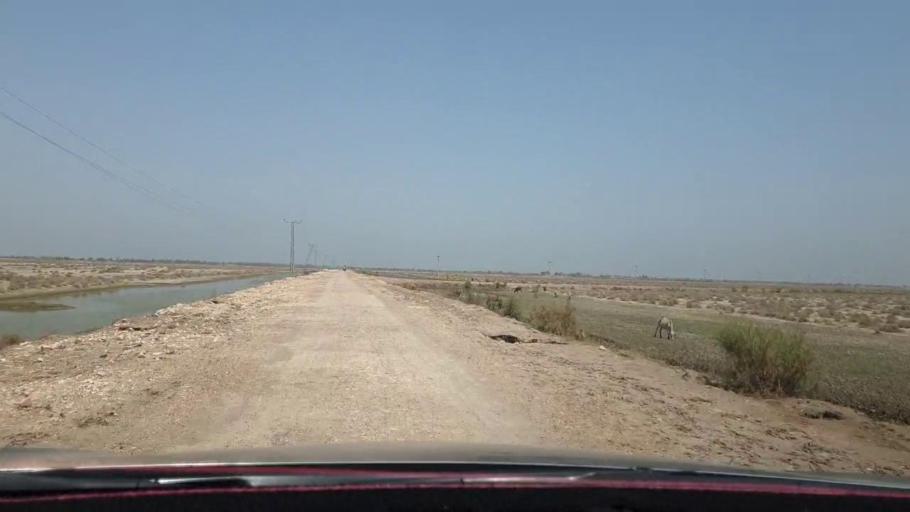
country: PK
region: Sindh
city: Warah
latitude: 27.3826
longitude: 67.6780
